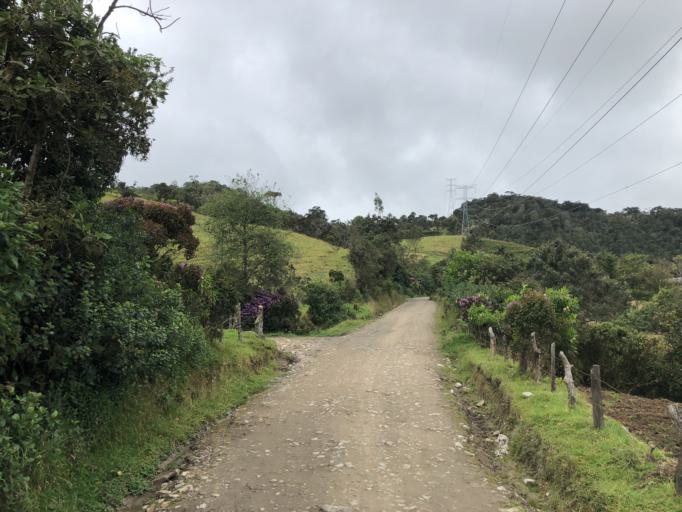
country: CO
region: Cauca
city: Totoro
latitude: 2.4976
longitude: -76.3513
